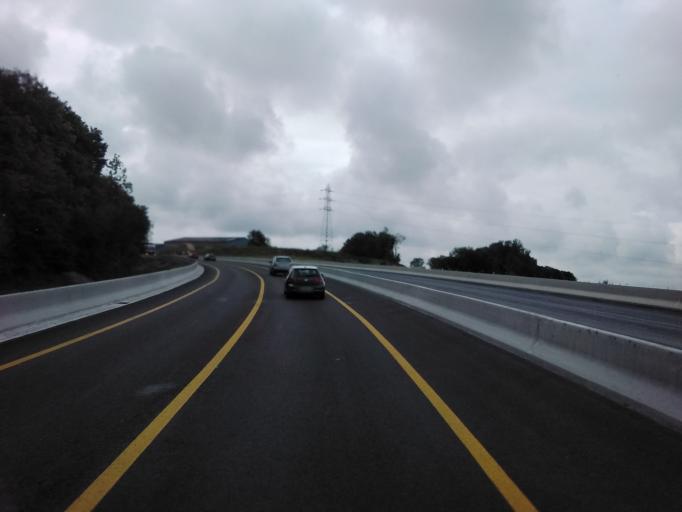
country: FR
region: Franche-Comte
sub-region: Departement du Doubs
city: Miserey-Salines
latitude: 47.2842
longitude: 5.9844
